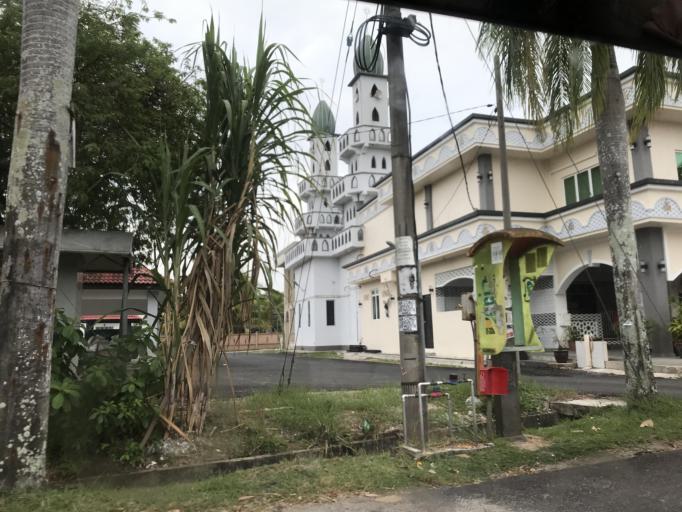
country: MY
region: Kelantan
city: Kota Bharu
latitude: 6.1145
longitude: 102.2121
